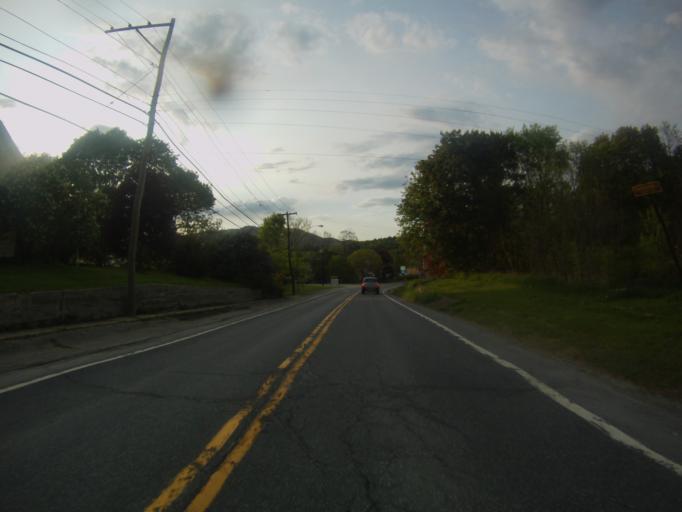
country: US
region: New York
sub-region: Essex County
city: Port Henry
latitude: 43.9536
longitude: -73.4325
